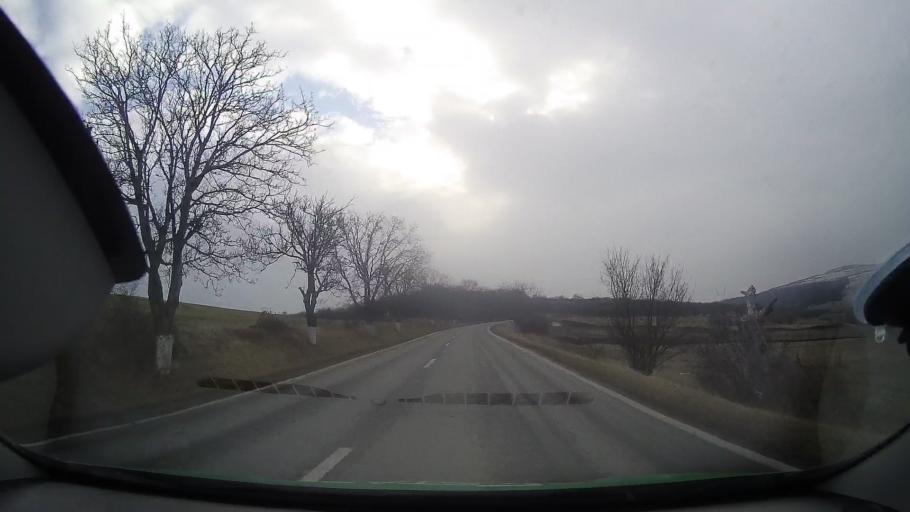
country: RO
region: Mures
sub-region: Municipiul Tarnaveni
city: Bobohalma
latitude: 46.3547
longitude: 24.2669
